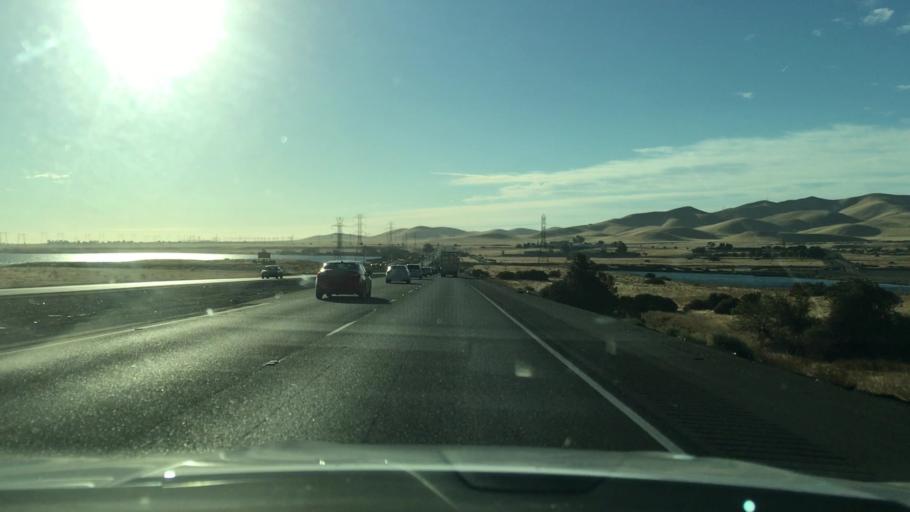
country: US
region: California
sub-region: Merced County
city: Gustine
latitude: 37.0718
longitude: -121.0763
